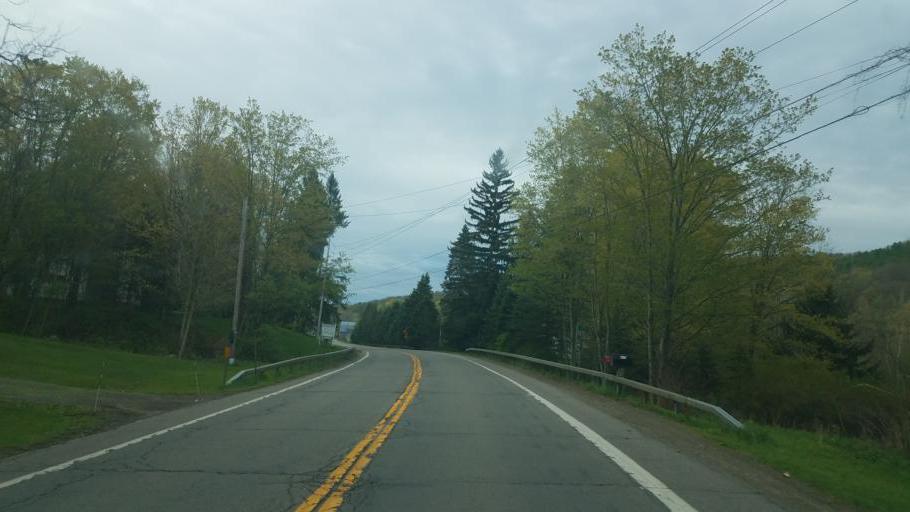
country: US
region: New York
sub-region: Steuben County
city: Canisteo
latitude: 42.2183
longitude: -77.5713
